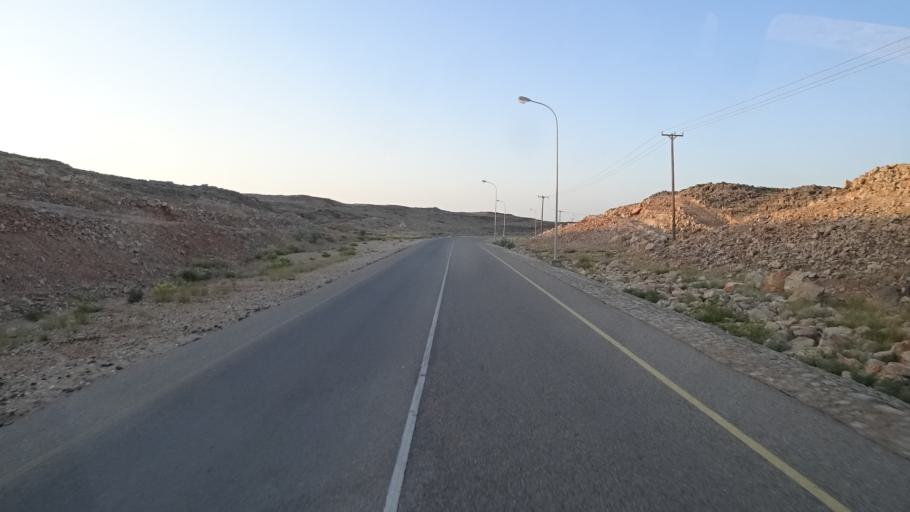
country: OM
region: Ash Sharqiyah
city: Sur
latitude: 22.5048
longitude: 59.7925
